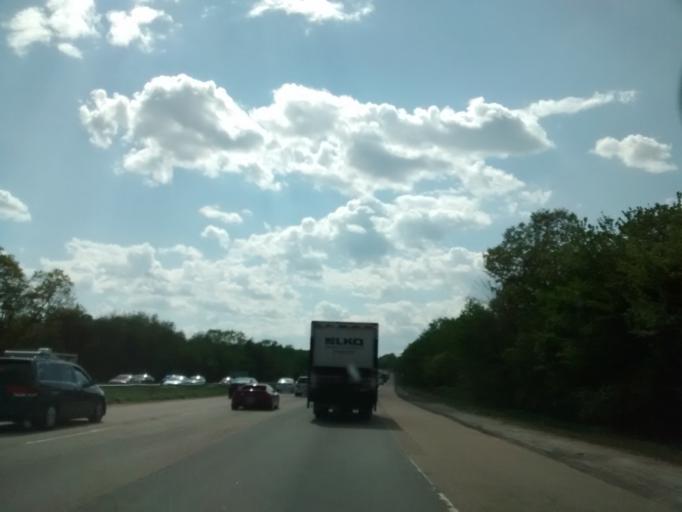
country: US
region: Massachusetts
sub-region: Worcester County
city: Millbury
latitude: 42.2066
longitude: -71.7919
